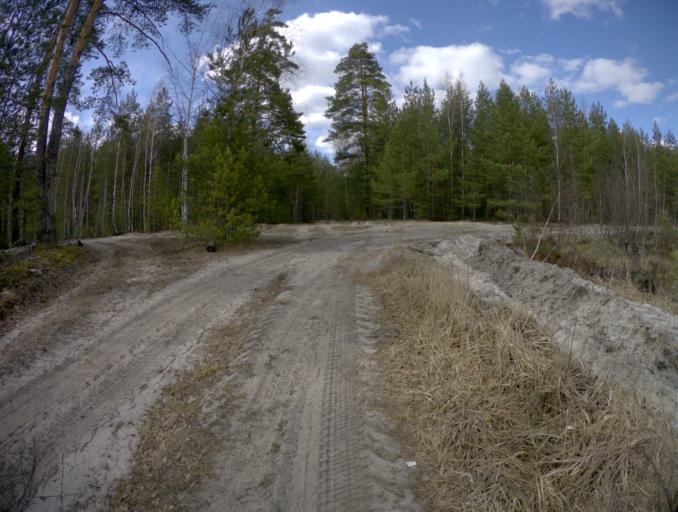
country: RU
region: Vladimir
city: Vorsha
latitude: 55.8879
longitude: 40.1744
